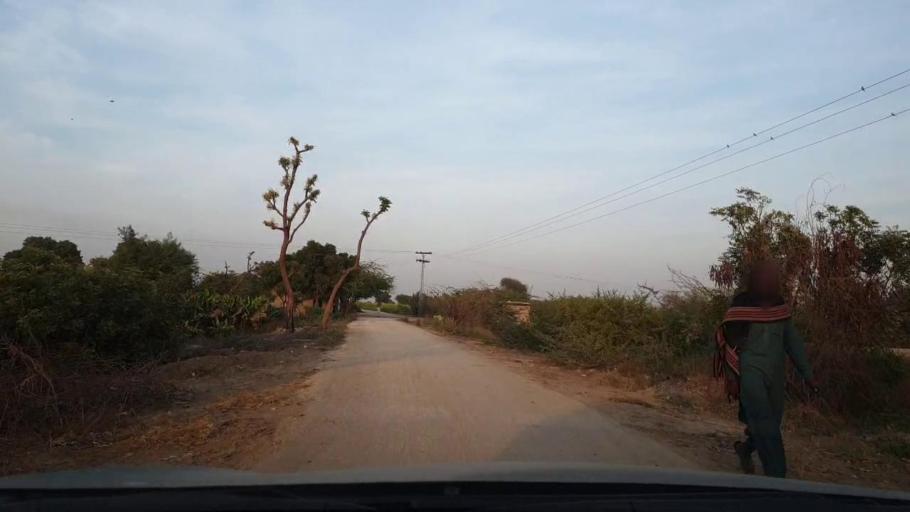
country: PK
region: Sindh
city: Tando Adam
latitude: 25.6805
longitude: 68.7129
